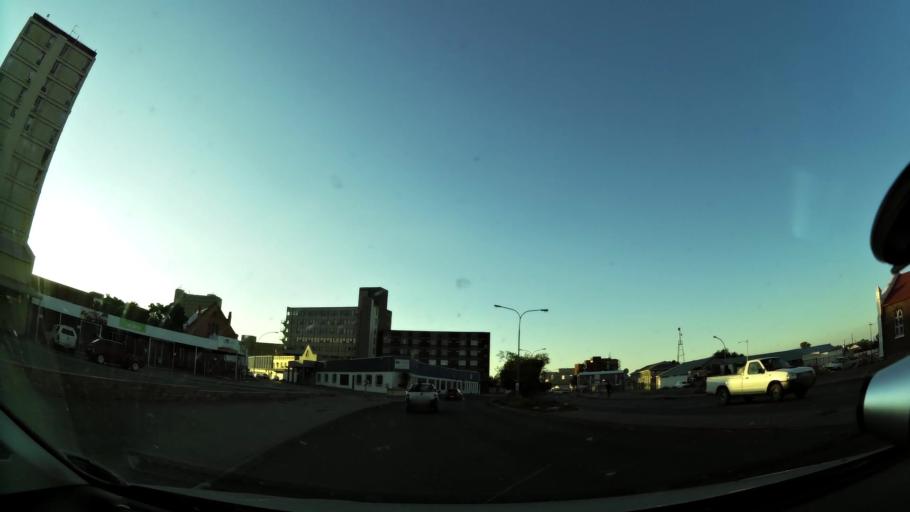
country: ZA
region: Northern Cape
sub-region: Frances Baard District Municipality
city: Kimberley
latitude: -28.7406
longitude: 24.7683
